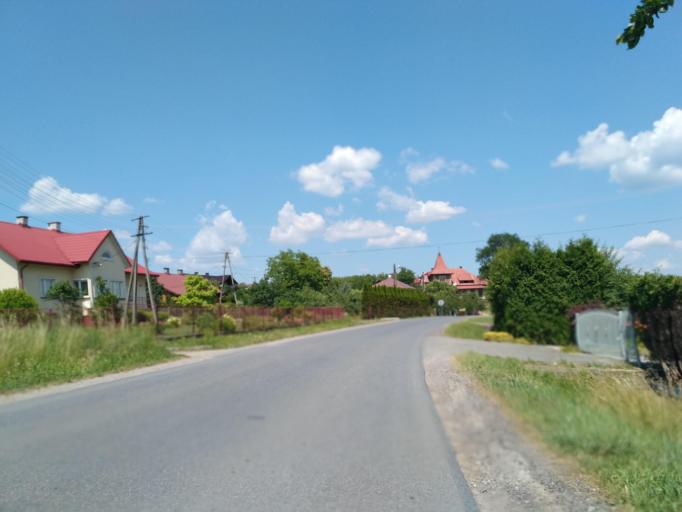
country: PL
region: Subcarpathian Voivodeship
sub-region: Powiat sanocki
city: Niebieszczany
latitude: 49.5547
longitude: 22.1439
